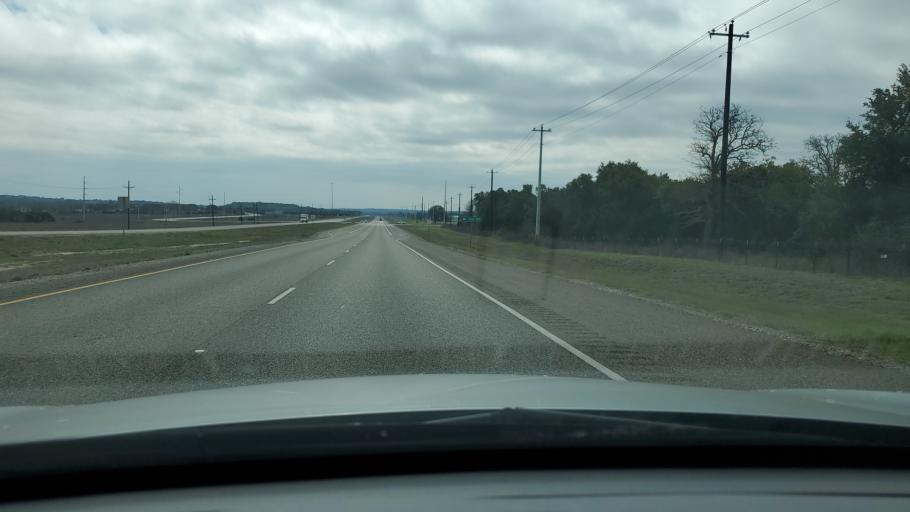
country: US
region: Texas
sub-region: Williamson County
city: Florence
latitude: 30.7922
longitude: -97.7667
